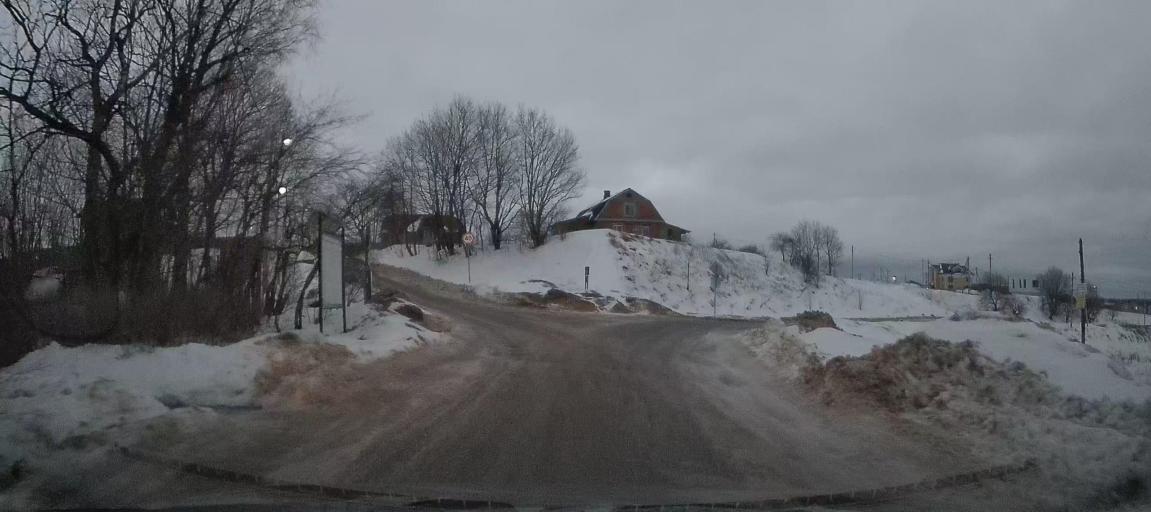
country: RU
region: Leningrad
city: Taytsy
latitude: 59.6949
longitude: 30.1459
